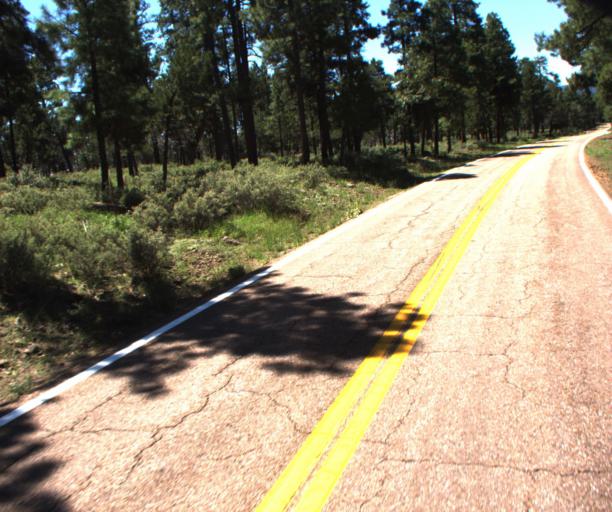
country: US
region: Arizona
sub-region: Greenlee County
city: Morenci
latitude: 33.5057
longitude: -109.3230
